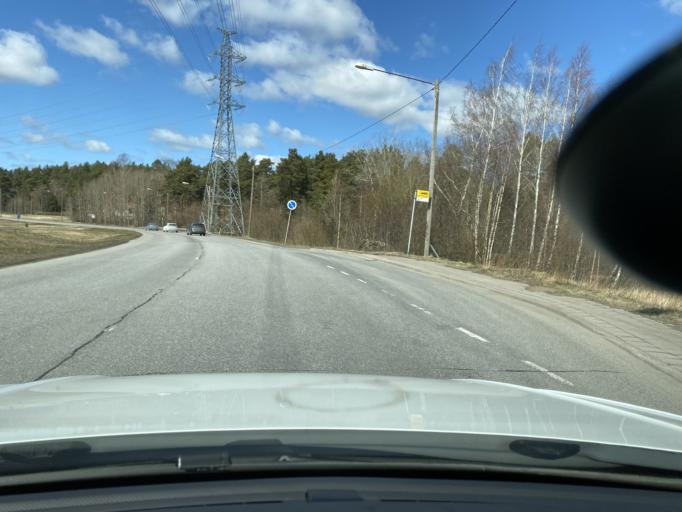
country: FI
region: Varsinais-Suomi
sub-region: Turku
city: Turku
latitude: 60.4743
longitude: 22.2803
